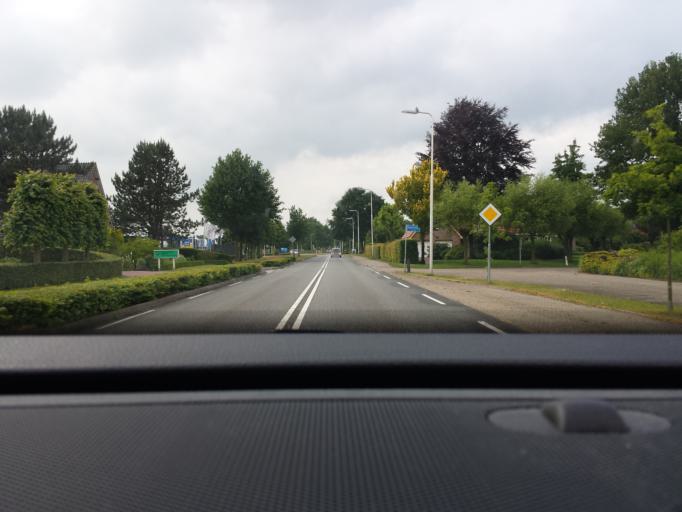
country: NL
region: Gelderland
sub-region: Gemeente Lochem
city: Barchem
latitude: 52.0801
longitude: 6.4606
